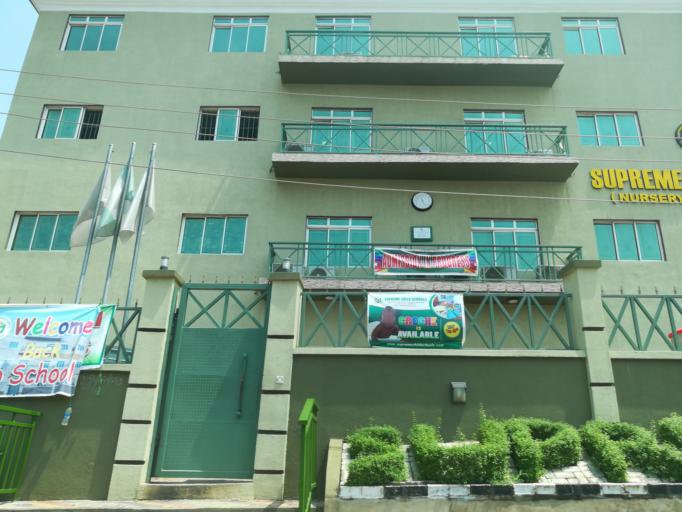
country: NG
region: Lagos
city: Ikorodu
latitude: 6.6210
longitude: 3.4948
